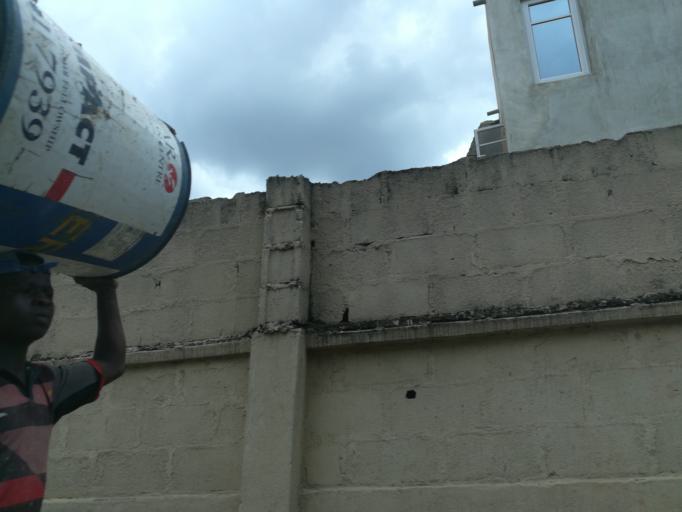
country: NG
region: Lagos
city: Ikeja
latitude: 6.6029
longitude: 3.3479
